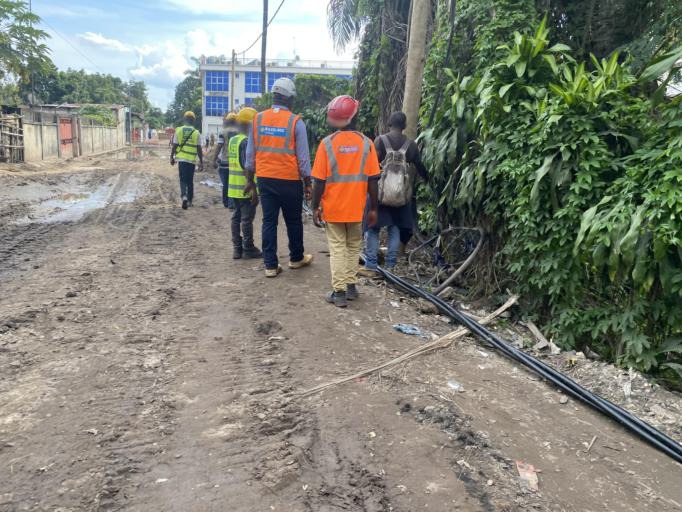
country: CG
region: Brazzaville
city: Brazzaville
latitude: -4.2859
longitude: 15.2494
